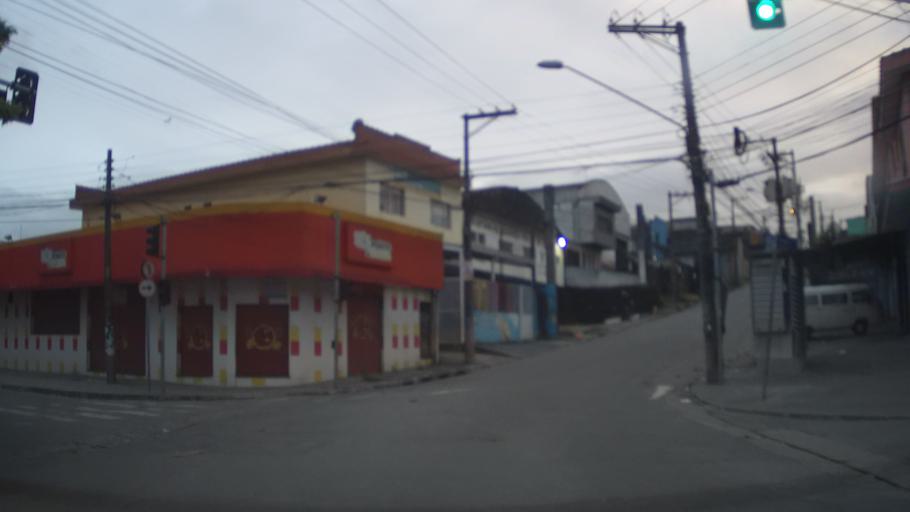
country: BR
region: Sao Paulo
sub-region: Guarulhos
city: Guarulhos
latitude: -23.4626
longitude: -46.4667
